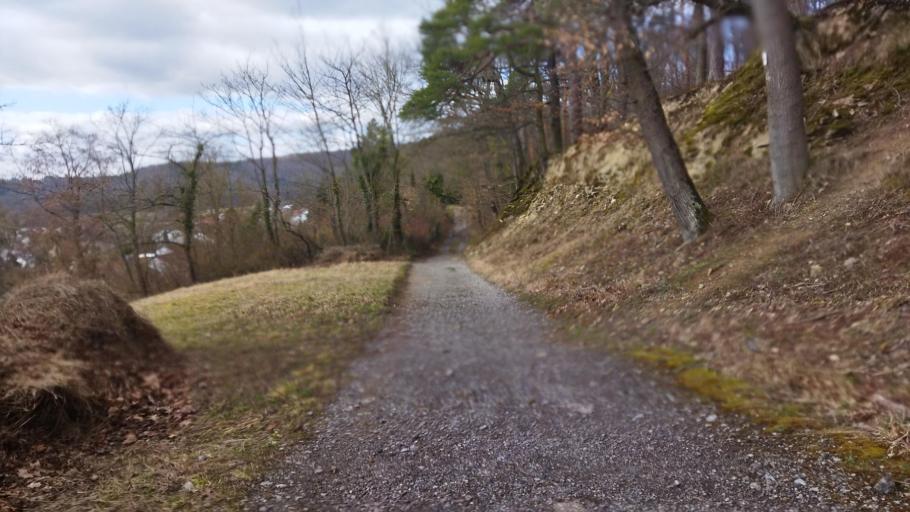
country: DE
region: Baden-Wuerttemberg
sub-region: Regierungsbezirk Stuttgart
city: Freudental
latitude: 49.0097
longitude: 9.0687
